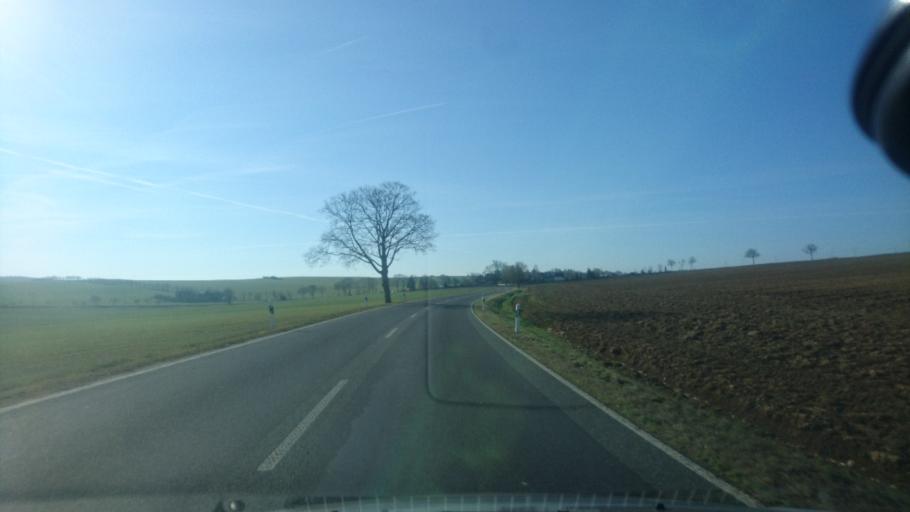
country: DE
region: Saxony
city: Neuensalz
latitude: 50.4927
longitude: 12.2202
